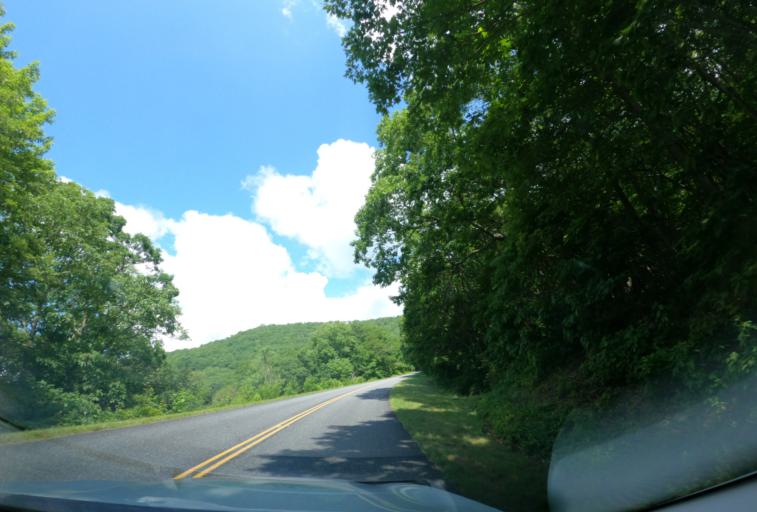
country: US
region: North Carolina
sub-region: Haywood County
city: Maggie Valley
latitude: 35.4488
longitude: -83.1079
